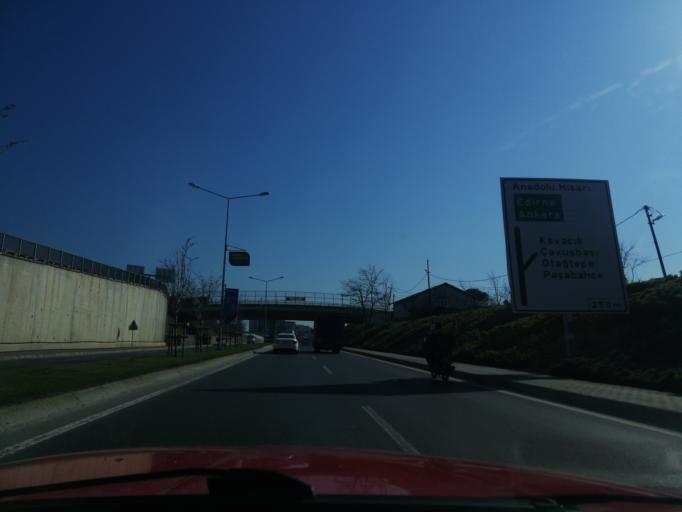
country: TR
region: Istanbul
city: Umraniye
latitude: 41.1007
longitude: 29.0973
